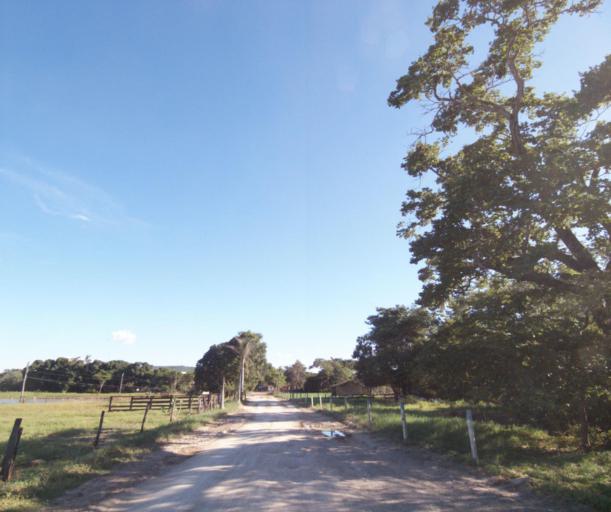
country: BR
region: Minas Gerais
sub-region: Manga
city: Manga
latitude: -14.3108
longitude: -44.4616
